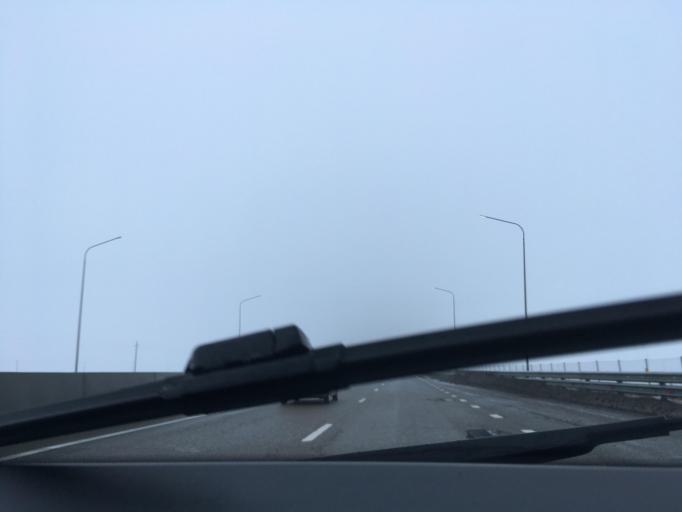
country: RU
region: Krasnodarskiy
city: Krasnoye
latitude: 46.7856
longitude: 39.6657
